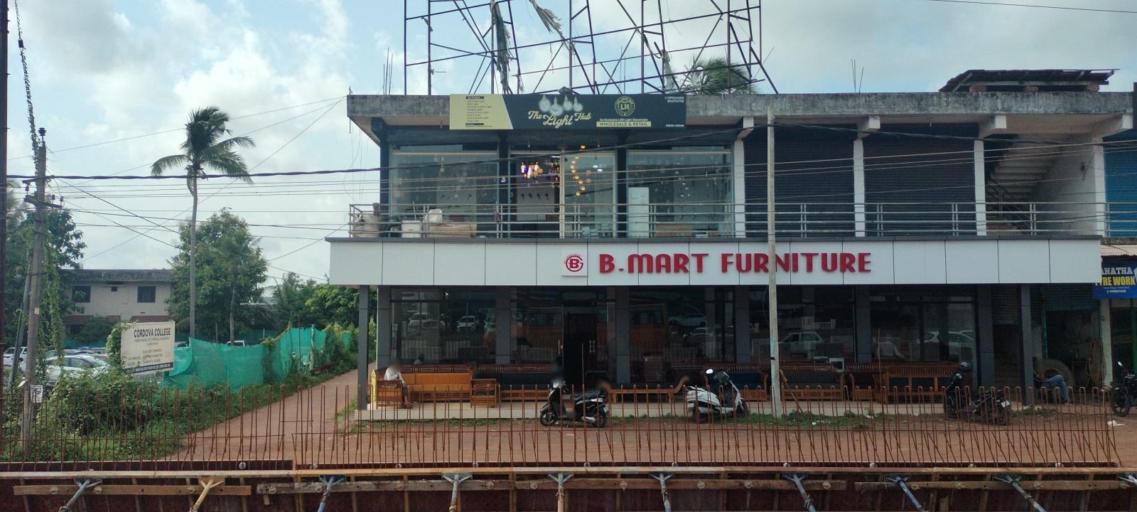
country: IN
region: Kerala
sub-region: Kasaragod District
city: Kasaragod
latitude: 12.5098
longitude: 75.0458
